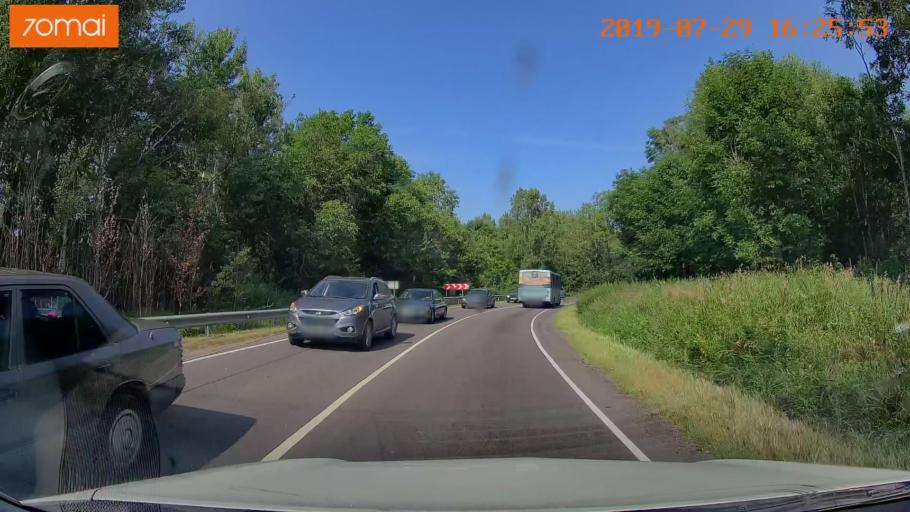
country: RU
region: Kaliningrad
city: Primorsk
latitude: 54.7262
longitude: 19.9703
